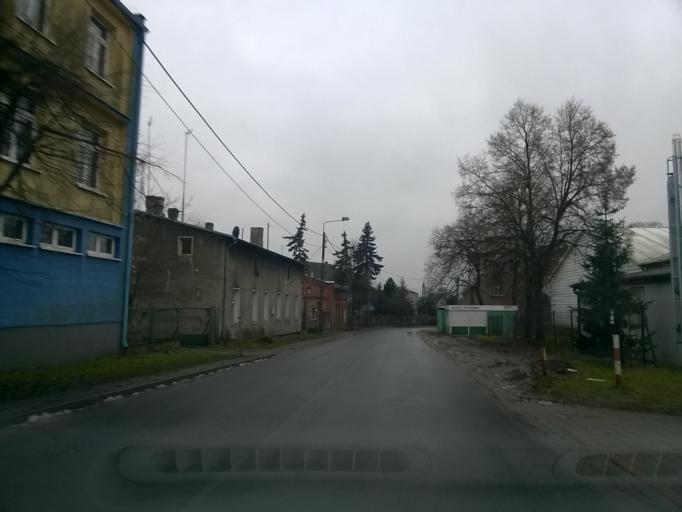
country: PL
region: Kujawsko-Pomorskie
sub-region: Powiat nakielski
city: Naklo nad Notecia
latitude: 53.1341
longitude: 17.5811
